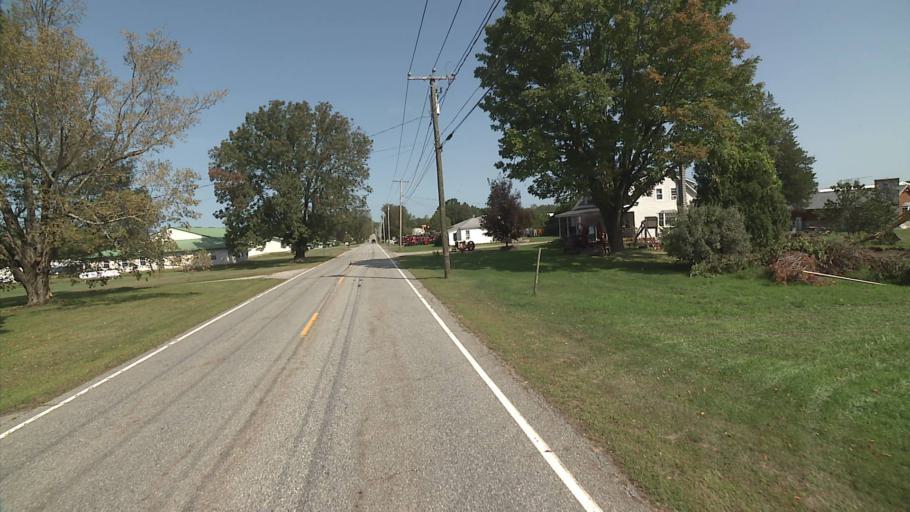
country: US
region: Connecticut
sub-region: Windham County
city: East Brooklyn
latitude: 41.8331
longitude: -71.9587
